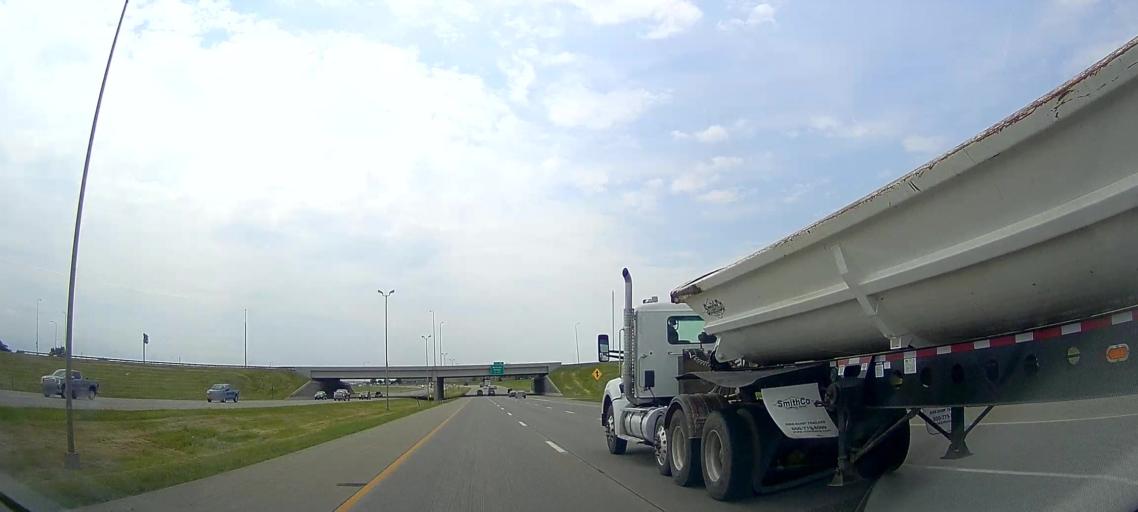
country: US
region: South Dakota
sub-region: Minnehaha County
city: Sioux Falls
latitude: 43.5739
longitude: -96.7741
